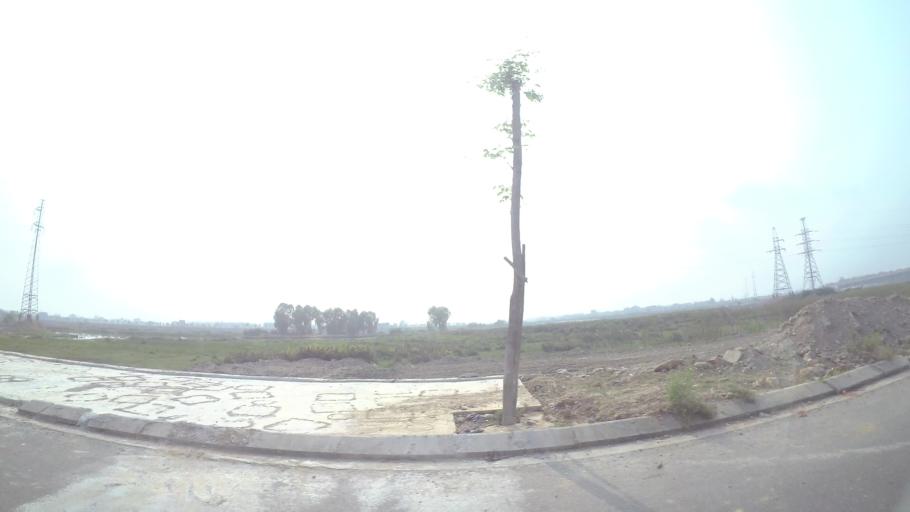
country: VN
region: Da Nang
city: Ngu Hanh Son
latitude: 16.0065
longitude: 108.2298
